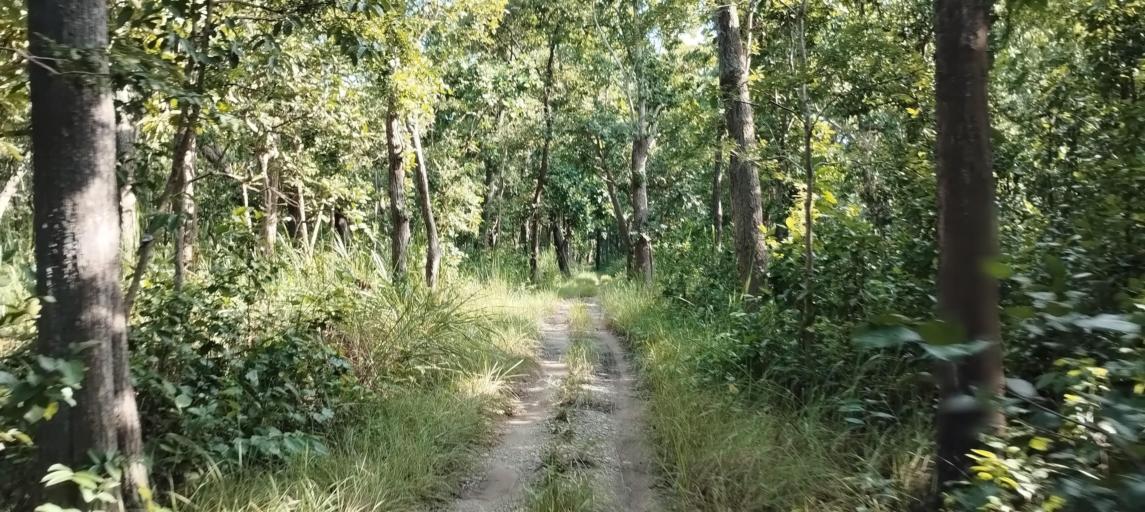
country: NP
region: Far Western
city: Tikapur
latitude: 28.5337
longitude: 81.2830
